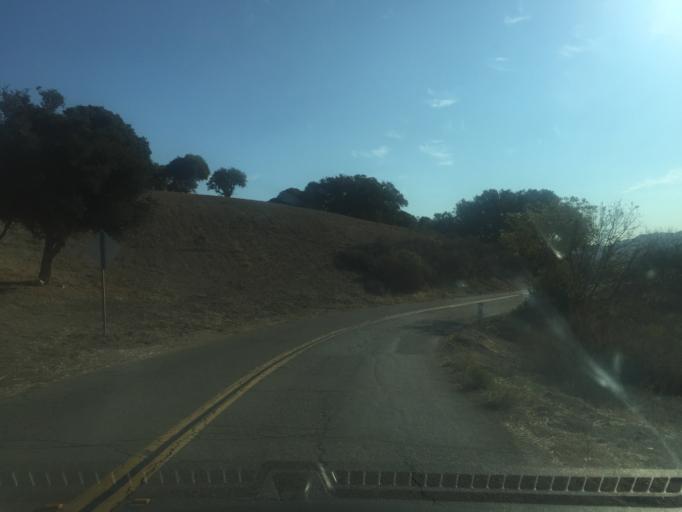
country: US
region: California
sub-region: Santa Barbara County
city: Lompoc
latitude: 34.5146
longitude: -120.4582
